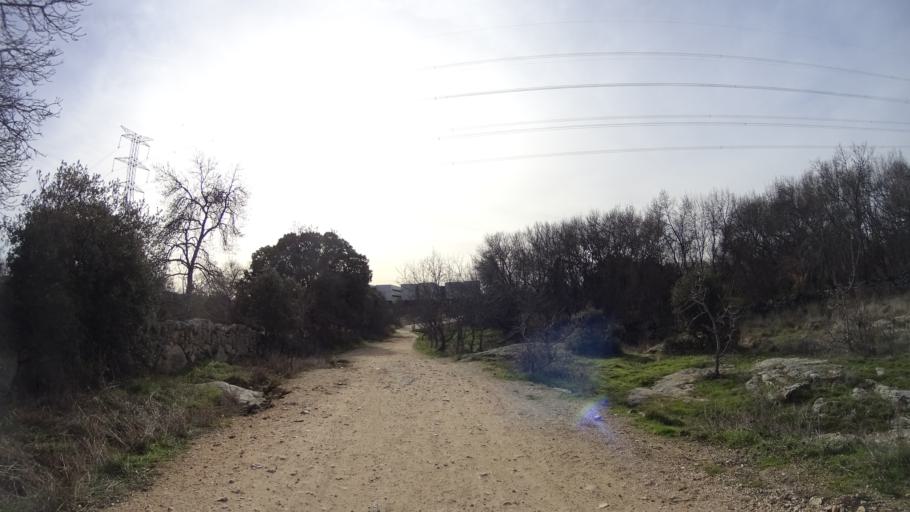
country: ES
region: Madrid
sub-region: Provincia de Madrid
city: Collado-Villalba
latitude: 40.6575
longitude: -3.9994
